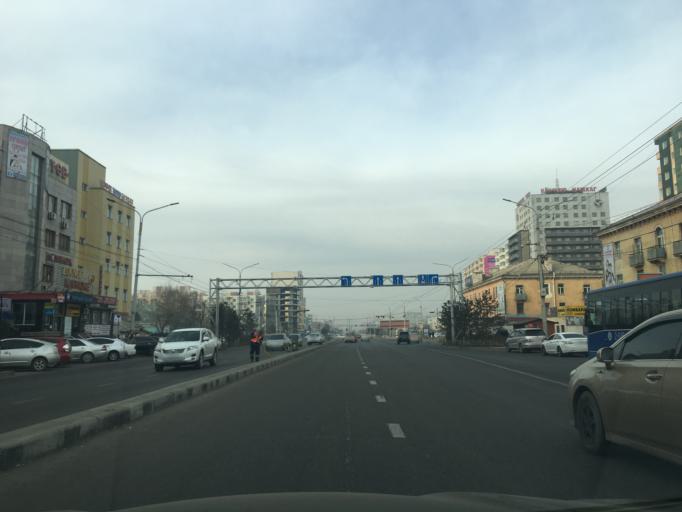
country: MN
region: Ulaanbaatar
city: Ulaanbaatar
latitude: 47.9146
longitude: 106.8789
